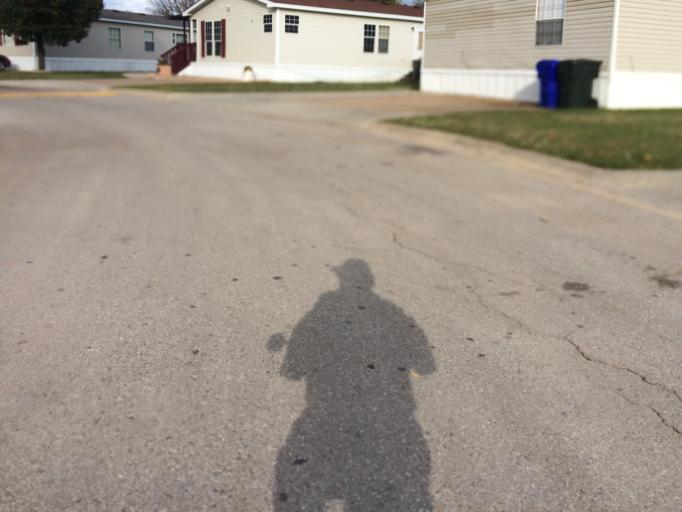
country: US
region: Oklahoma
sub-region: Cleveland County
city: Norman
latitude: 35.2381
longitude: -97.4533
